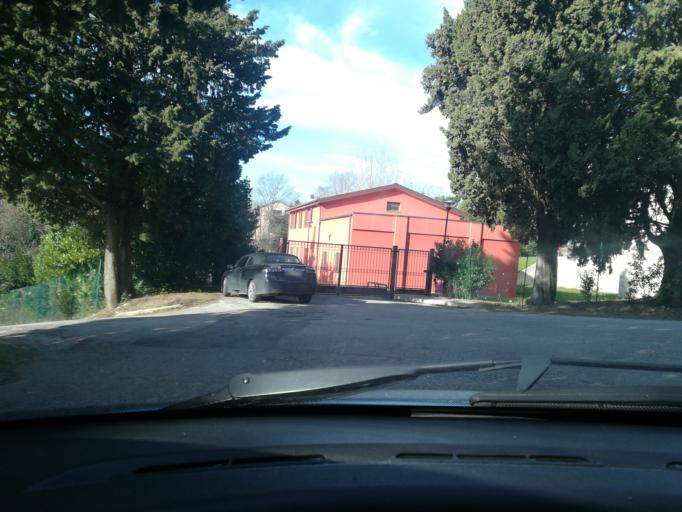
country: IT
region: The Marches
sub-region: Provincia di Macerata
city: Macerata
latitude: 43.2978
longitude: 13.4334
